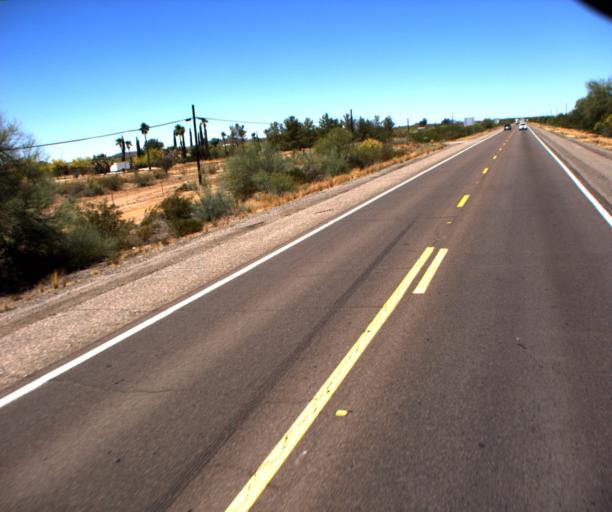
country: US
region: Arizona
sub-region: Maricopa County
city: Wickenburg
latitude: 34.0049
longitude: -112.7751
